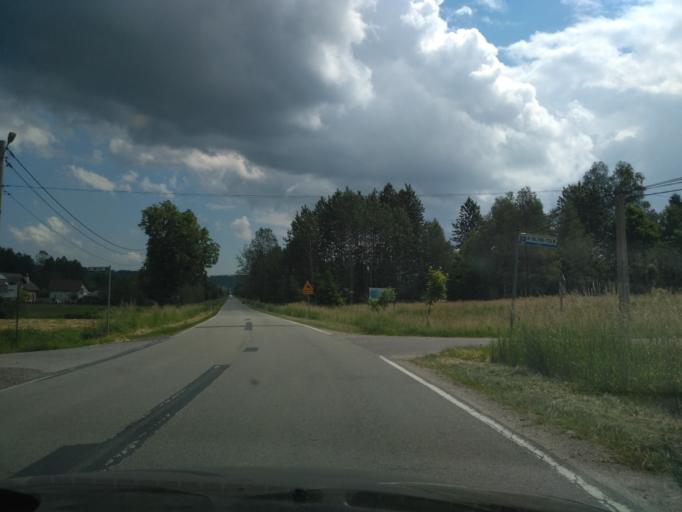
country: PL
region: Subcarpathian Voivodeship
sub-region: Powiat rzeszowski
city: Blazowa
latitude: 49.9263
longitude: 22.1266
